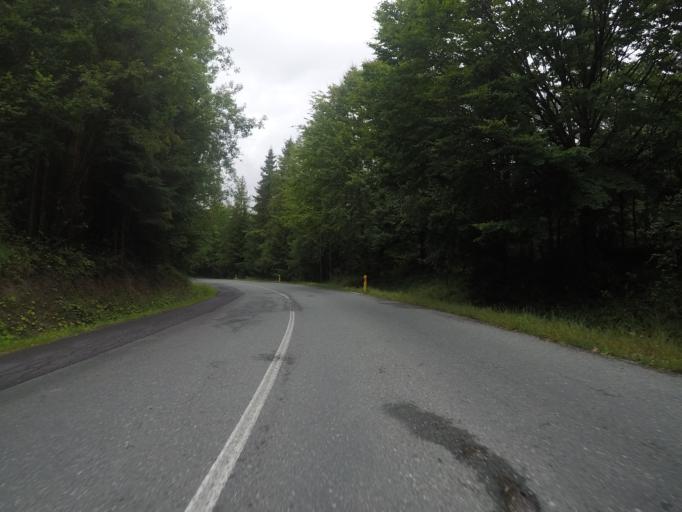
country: SK
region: Kosicky
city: Spisska Nova Ves
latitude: 48.8926
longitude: 20.5332
